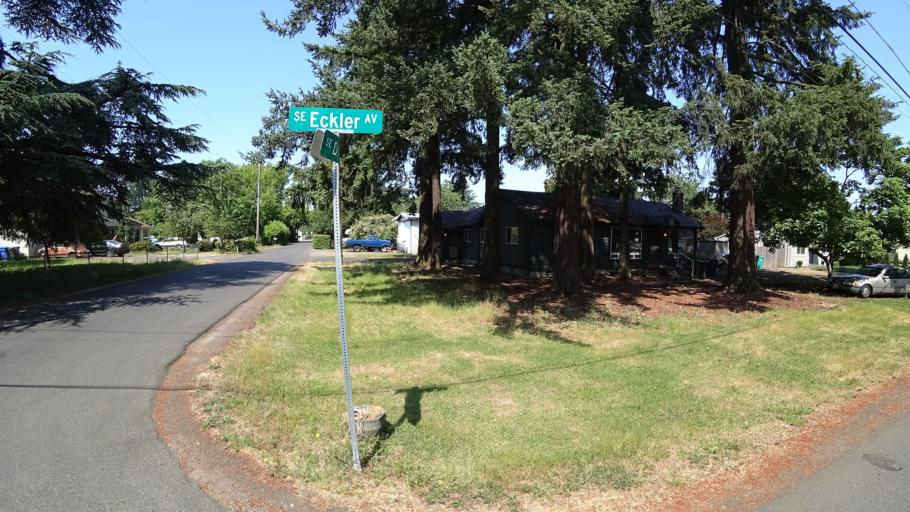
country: US
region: Oregon
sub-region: Multnomah County
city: Lents
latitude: 45.4512
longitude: -122.5907
